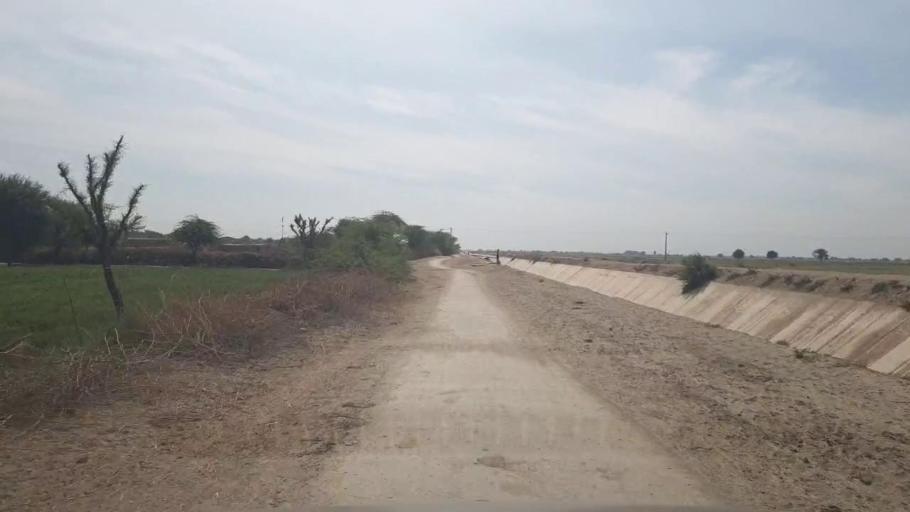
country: PK
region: Sindh
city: Umarkot
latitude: 25.3249
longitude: 69.6019
